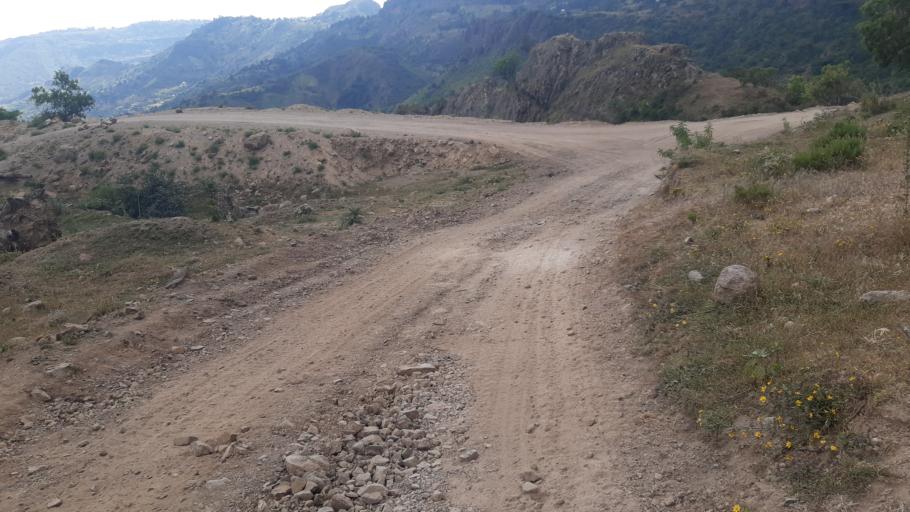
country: ET
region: Amhara
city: Dabat
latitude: 13.3413
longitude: 37.4039
